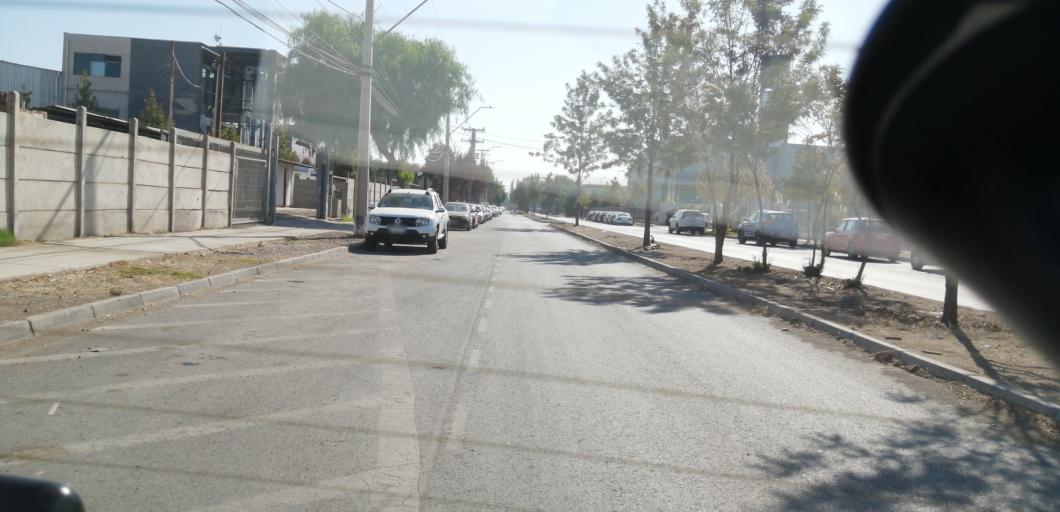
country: CL
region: Santiago Metropolitan
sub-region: Provincia de Santiago
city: Lo Prado
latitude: -33.3851
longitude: -70.7762
